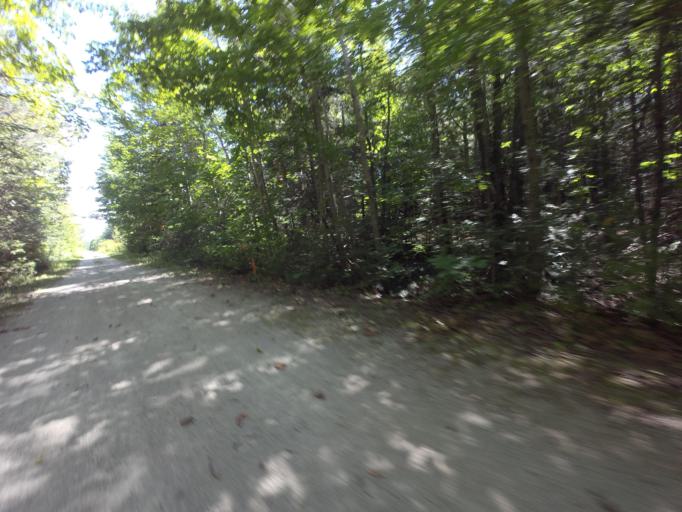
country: CA
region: Ontario
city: Orangeville
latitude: 43.7775
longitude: -80.1166
